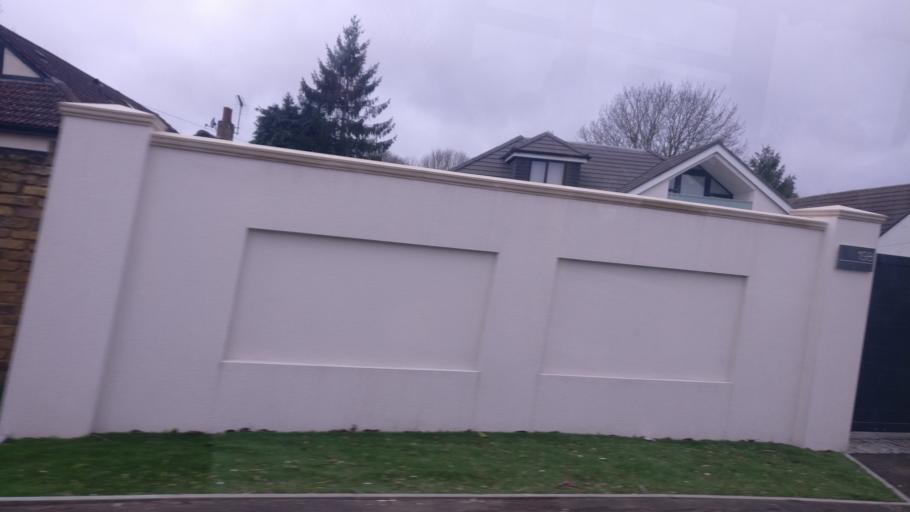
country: GB
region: England
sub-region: Surrey
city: Staines
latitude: 51.4157
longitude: -0.5132
